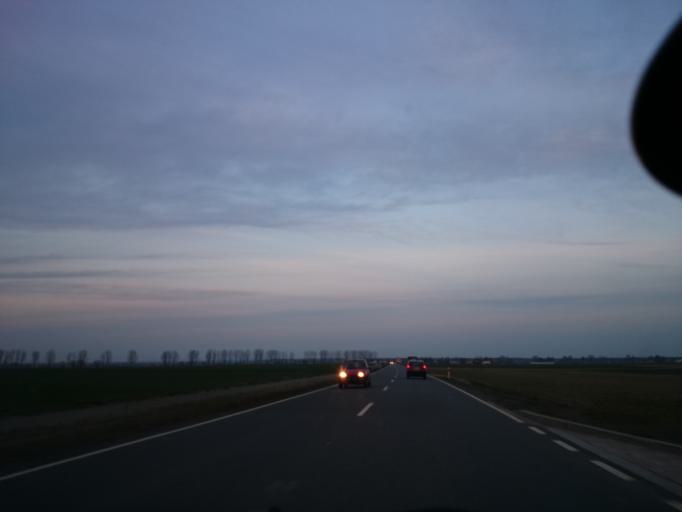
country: PL
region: Opole Voivodeship
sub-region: Powiat prudnicki
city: Biala
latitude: 50.4079
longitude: 17.7057
